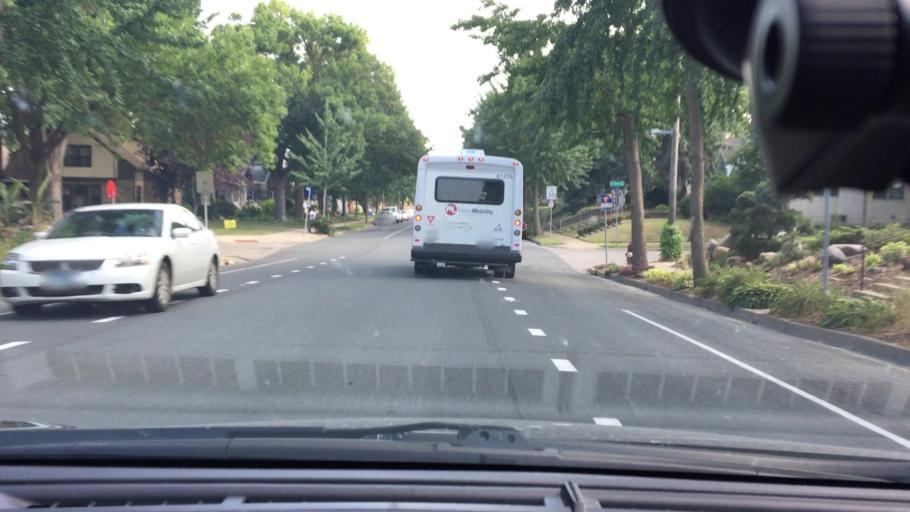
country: US
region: Minnesota
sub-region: Hennepin County
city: Richfield
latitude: 44.9110
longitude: -93.2525
